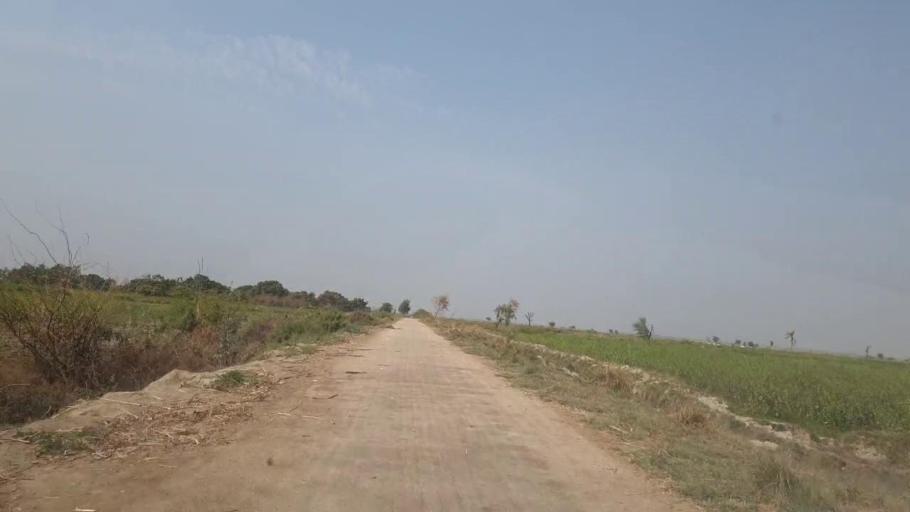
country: PK
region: Sindh
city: Mirpur Khas
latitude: 25.5829
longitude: 69.1366
